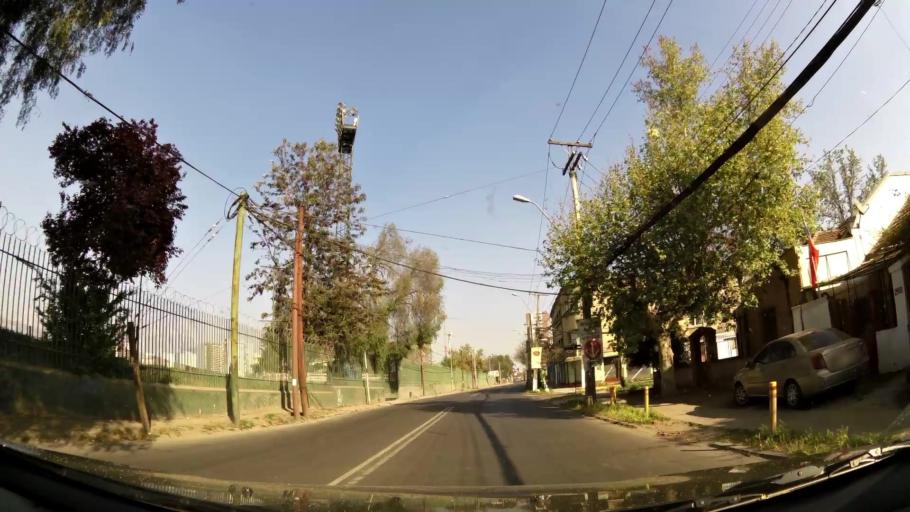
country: CL
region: Santiago Metropolitan
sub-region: Provincia de Santiago
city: Santiago
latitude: -33.4038
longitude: -70.6696
